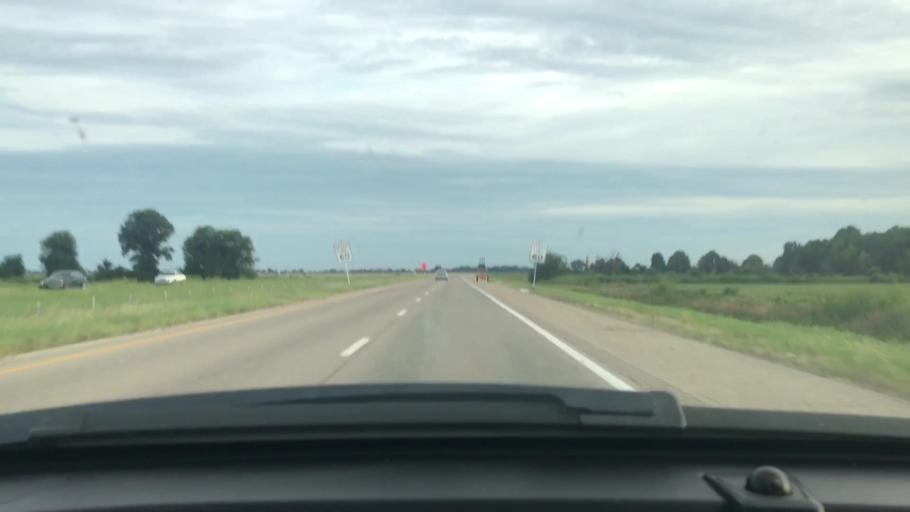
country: US
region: Arkansas
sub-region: Craighead County
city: Bay
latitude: 35.7216
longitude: -90.5802
